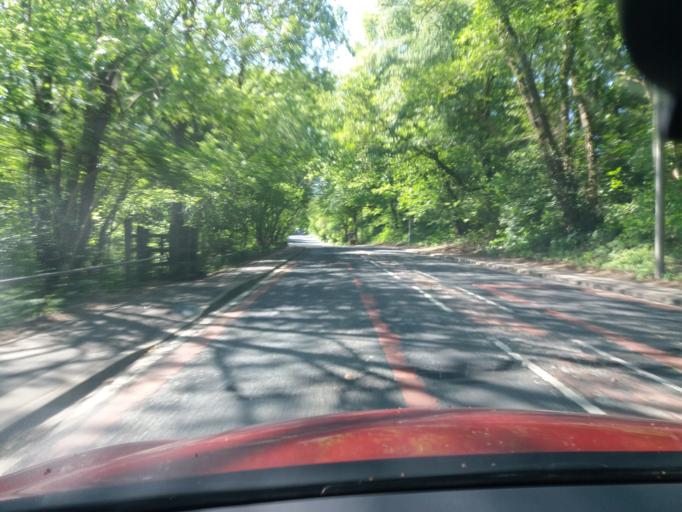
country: GB
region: England
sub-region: Lancashire
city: Coppull
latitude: 53.6333
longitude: -2.6549
